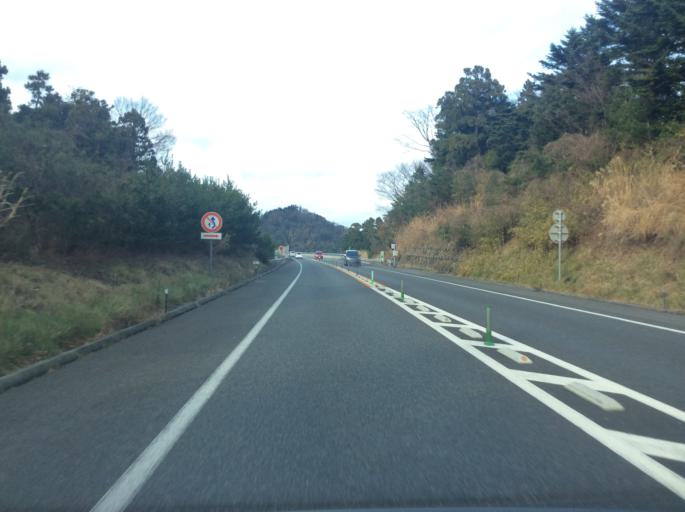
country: JP
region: Fukushima
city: Iwaki
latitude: 37.1976
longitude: 140.9864
